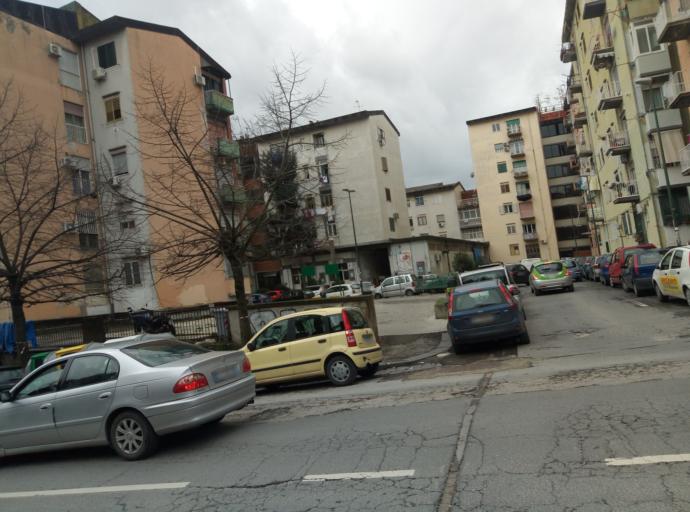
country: IT
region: Campania
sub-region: Provincia di Napoli
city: Napoli
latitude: 40.8606
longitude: 14.2248
